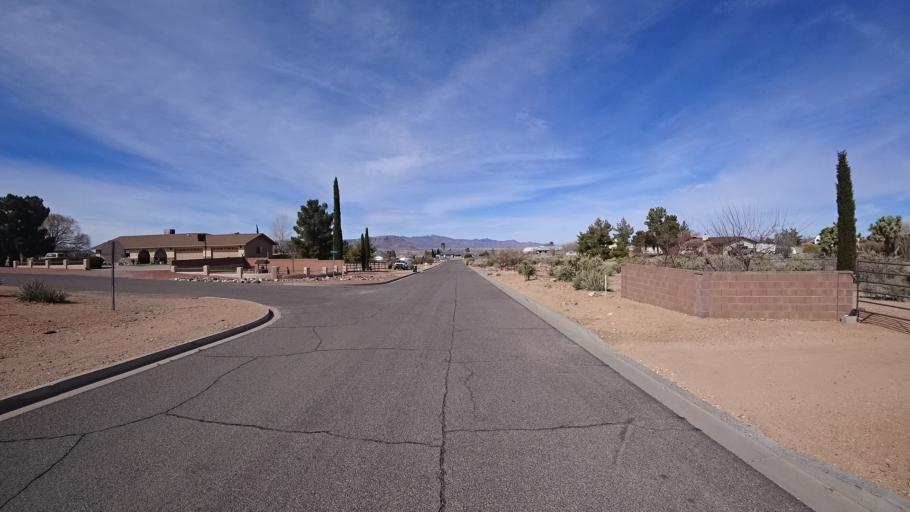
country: US
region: Arizona
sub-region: Mohave County
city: Kingman
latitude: 35.1843
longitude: -113.9894
